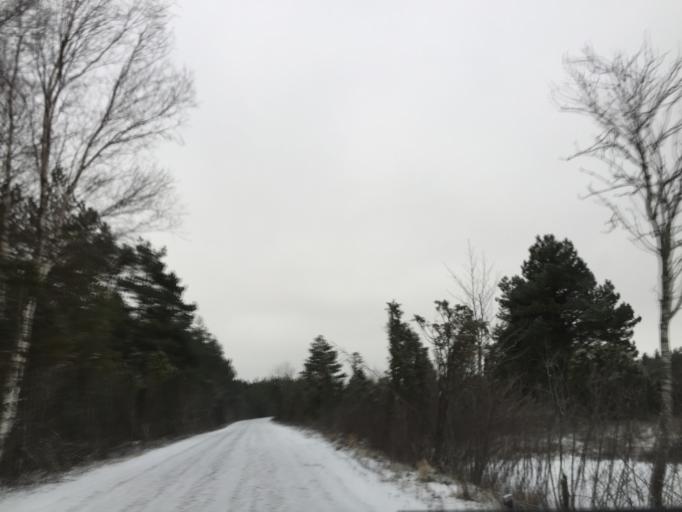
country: EE
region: Saare
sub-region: Orissaare vald
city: Orissaare
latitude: 58.5650
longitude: 23.3860
